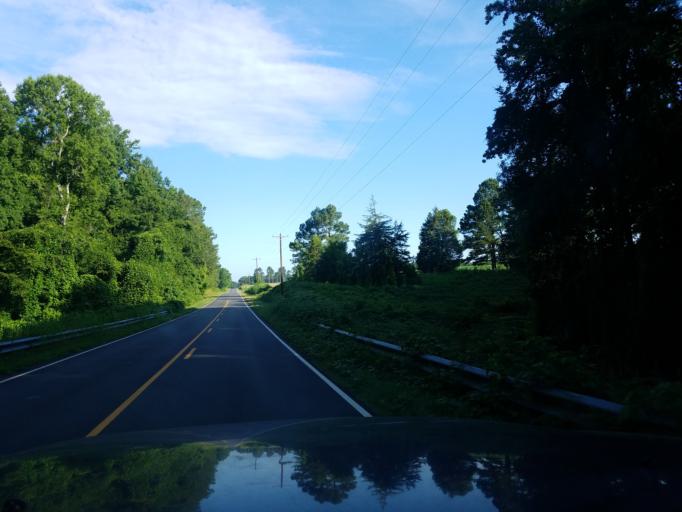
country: US
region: North Carolina
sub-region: Granville County
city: Butner
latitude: 36.1644
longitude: -78.7825
